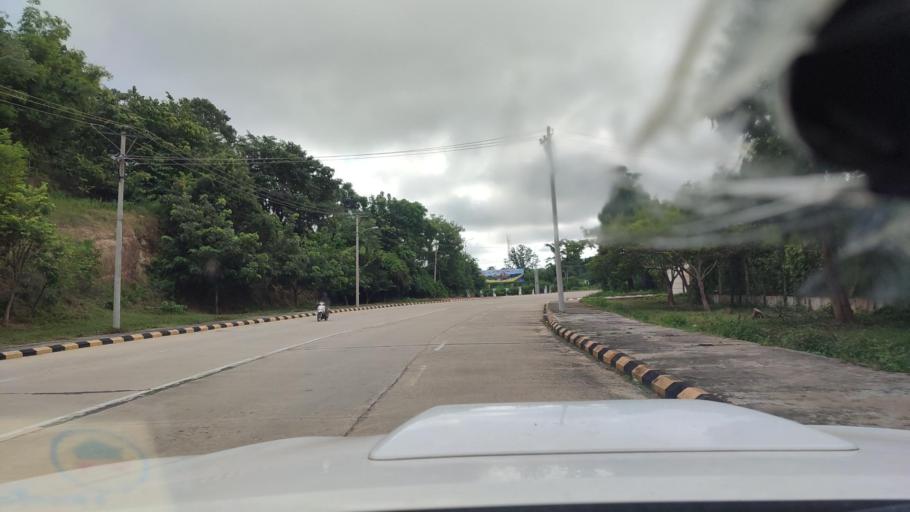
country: MM
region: Mandalay
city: Nay Pyi Taw
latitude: 19.7622
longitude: 96.0759
